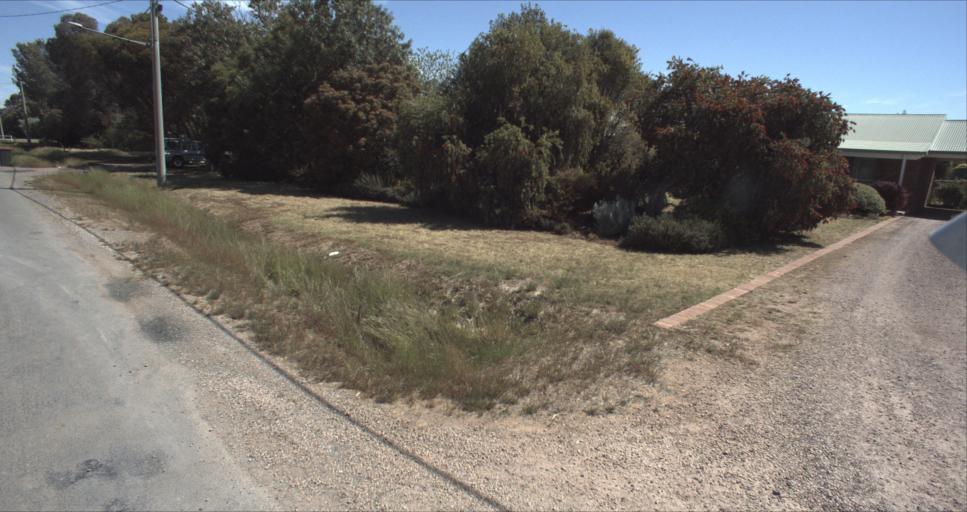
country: AU
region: New South Wales
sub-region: Leeton
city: Leeton
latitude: -34.5529
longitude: 146.3835
